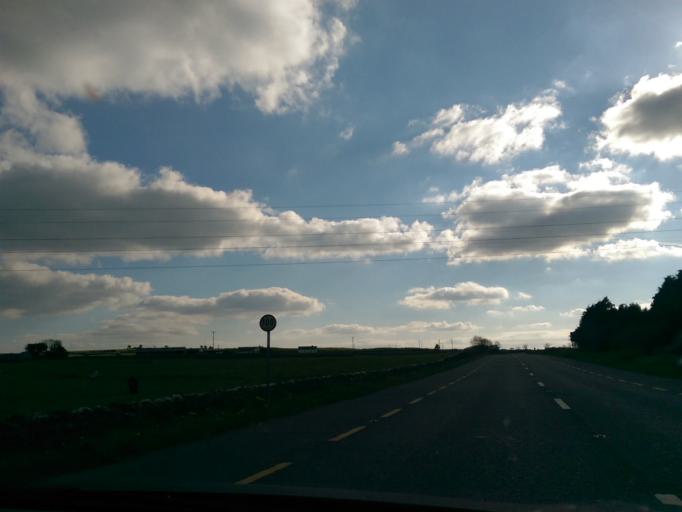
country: IE
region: Connaught
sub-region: County Galway
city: Loughrea
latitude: 53.2075
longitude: -8.5224
